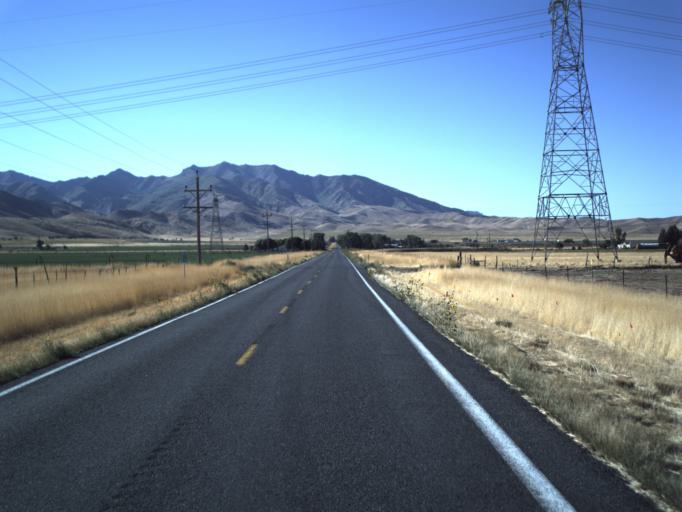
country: US
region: Utah
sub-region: Millard County
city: Delta
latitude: 39.4959
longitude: -112.2690
